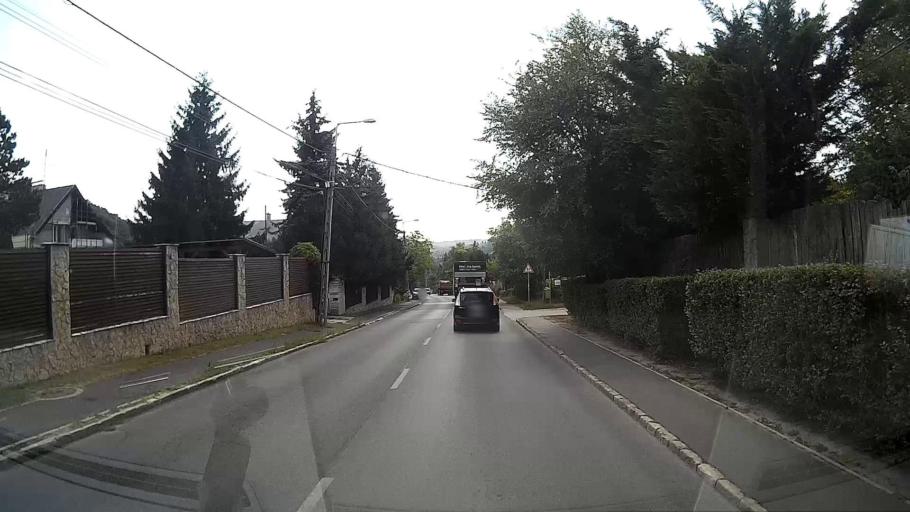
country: HU
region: Pest
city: Solymar
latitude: 47.5569
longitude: 18.9487
